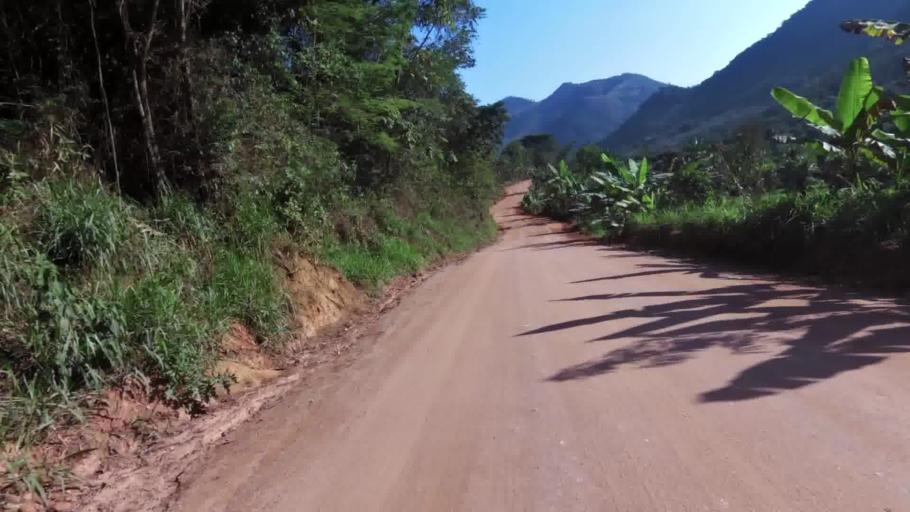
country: BR
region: Espirito Santo
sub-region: Alfredo Chaves
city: Alfredo Chaves
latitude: -20.6043
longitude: -40.7637
